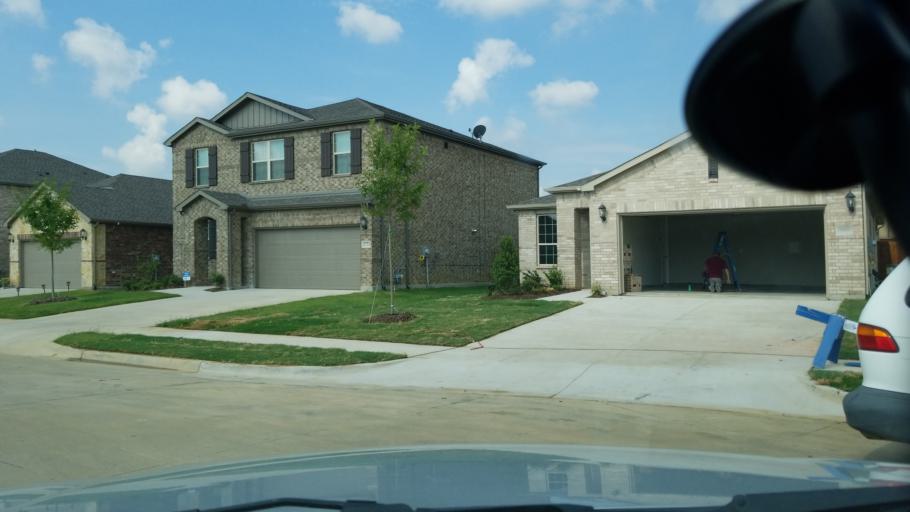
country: US
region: Texas
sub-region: Dallas County
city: Irving
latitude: 32.8437
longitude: -96.9195
